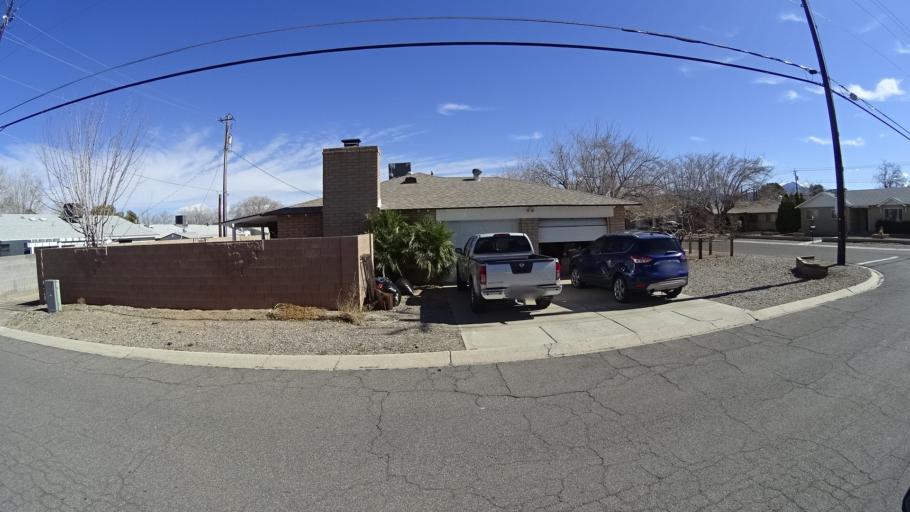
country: US
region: Arizona
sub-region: Mohave County
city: Kingman
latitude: 35.2114
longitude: -114.0401
